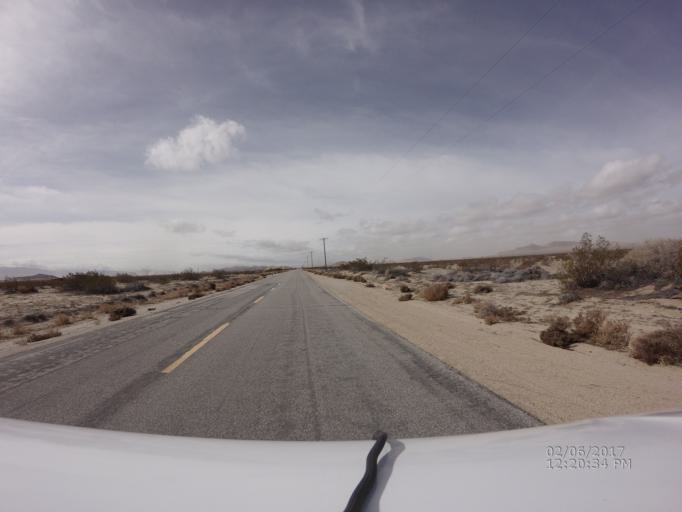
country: US
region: California
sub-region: Los Angeles County
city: Lake Los Angeles
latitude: 34.6165
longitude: -117.7347
